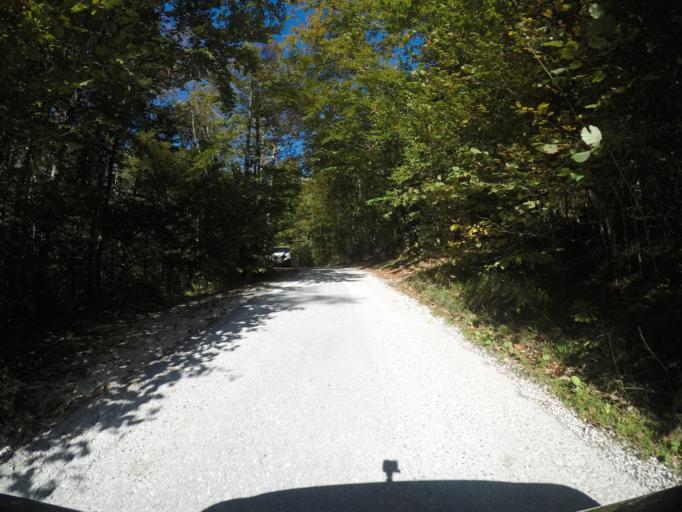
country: SI
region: Kamnik
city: Mekinje
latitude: 46.3285
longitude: 14.5886
